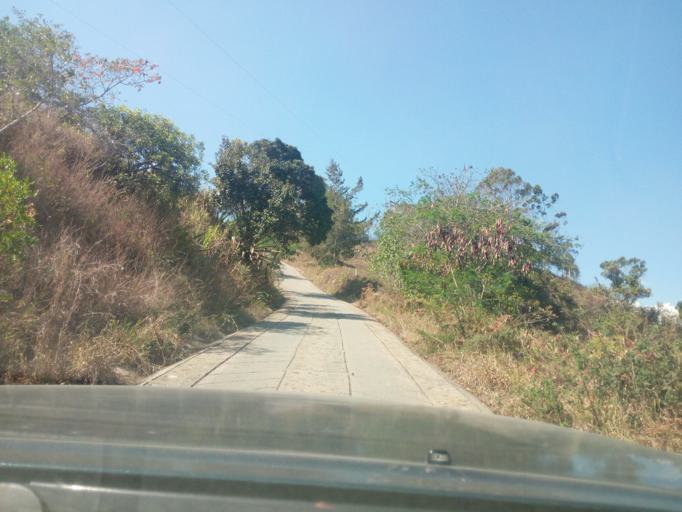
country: CO
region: Boyaca
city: Guateque
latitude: 4.9923
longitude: -73.4621
